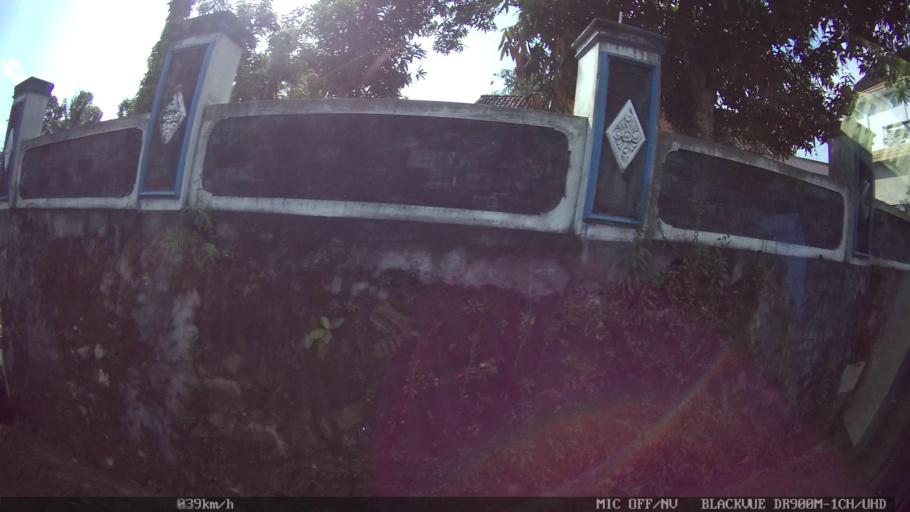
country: ID
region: Daerah Istimewa Yogyakarta
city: Kasihan
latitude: -7.8408
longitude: 110.3119
